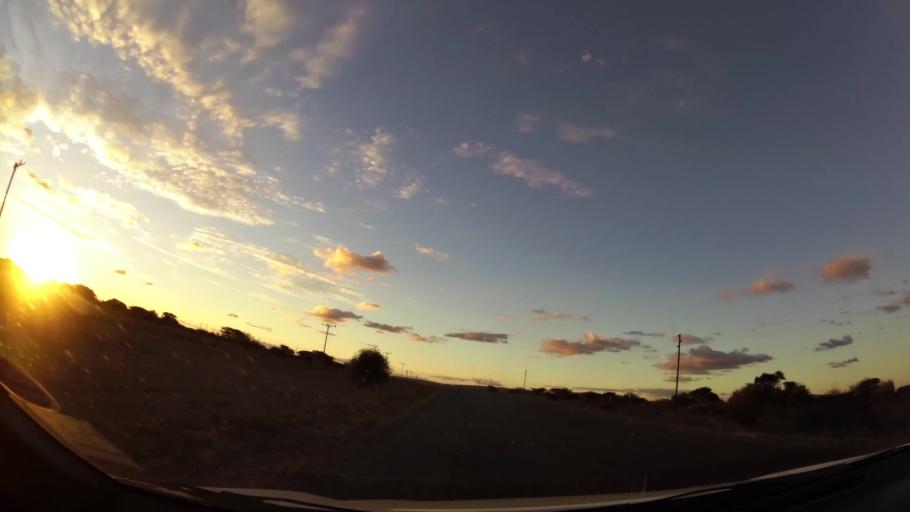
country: ZA
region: Limpopo
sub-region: Capricorn District Municipality
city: Polokwane
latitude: -23.7641
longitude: 29.4746
